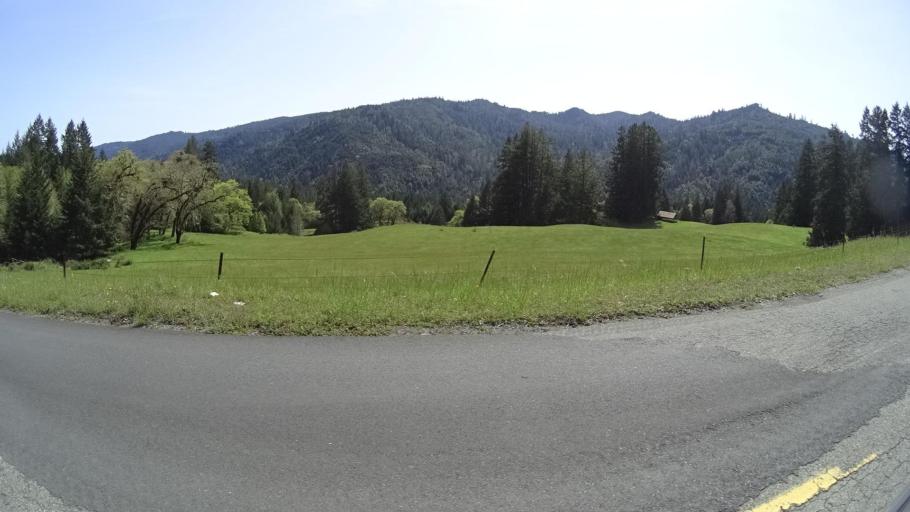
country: US
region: California
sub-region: Humboldt County
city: Redway
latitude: 40.3900
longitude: -123.7456
